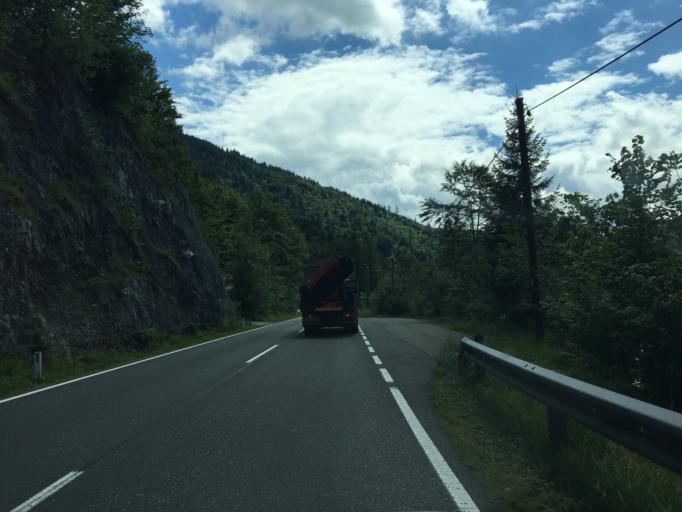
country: AT
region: Salzburg
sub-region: Politischer Bezirk Hallein
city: Krispl
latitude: 47.7481
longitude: 13.1732
